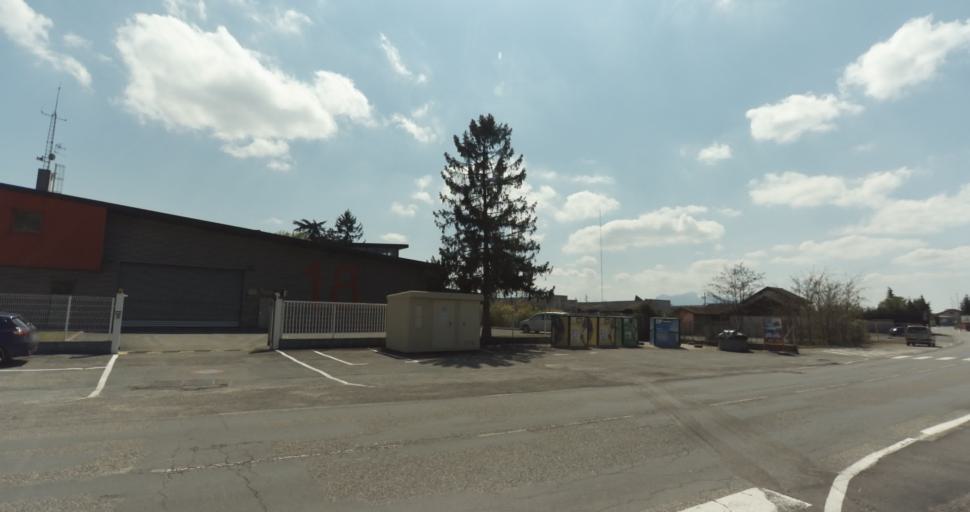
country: FR
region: Rhone-Alpes
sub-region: Departement de l'Isere
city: Saint-Marcellin
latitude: 45.1492
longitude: 5.3095
